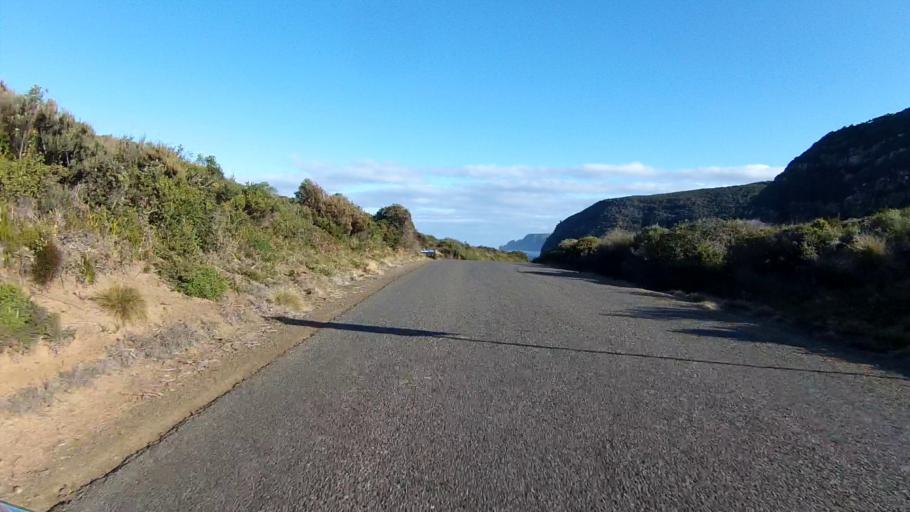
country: AU
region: Tasmania
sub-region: Clarence
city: Sandford
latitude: -43.1863
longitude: 147.8471
